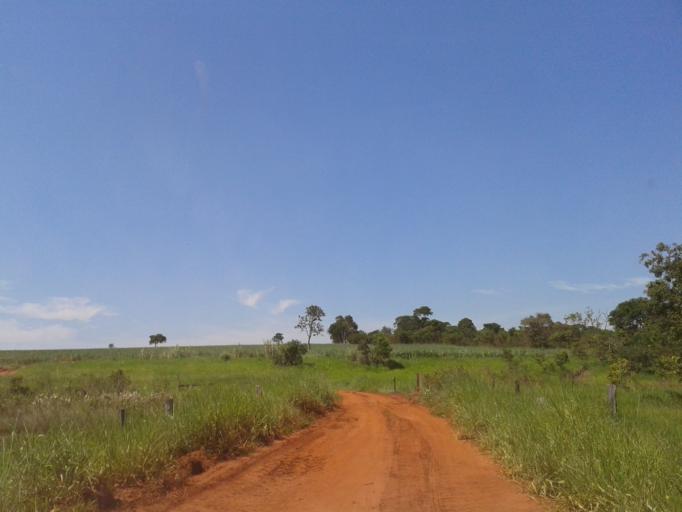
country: BR
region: Minas Gerais
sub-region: Santa Vitoria
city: Santa Vitoria
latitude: -19.0962
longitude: -50.4537
